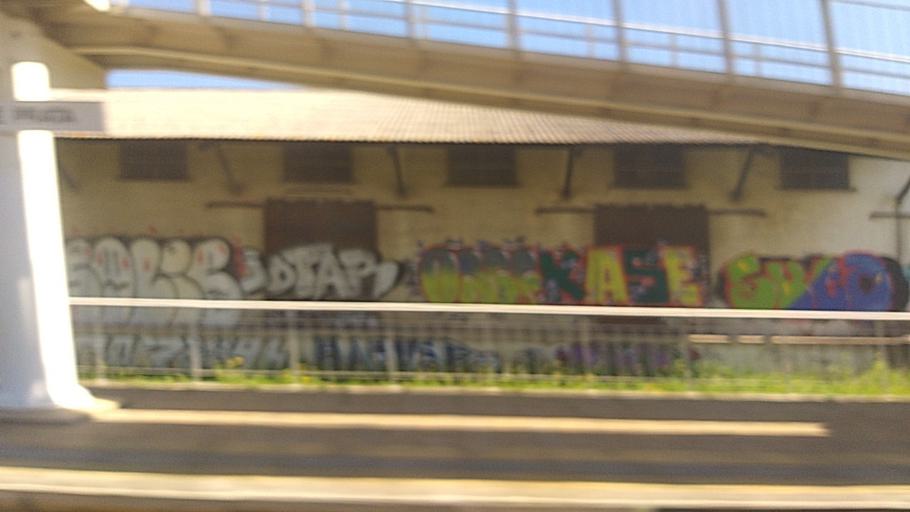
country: PT
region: Lisbon
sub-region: Loures
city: Moscavide
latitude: 38.7470
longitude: -9.1028
